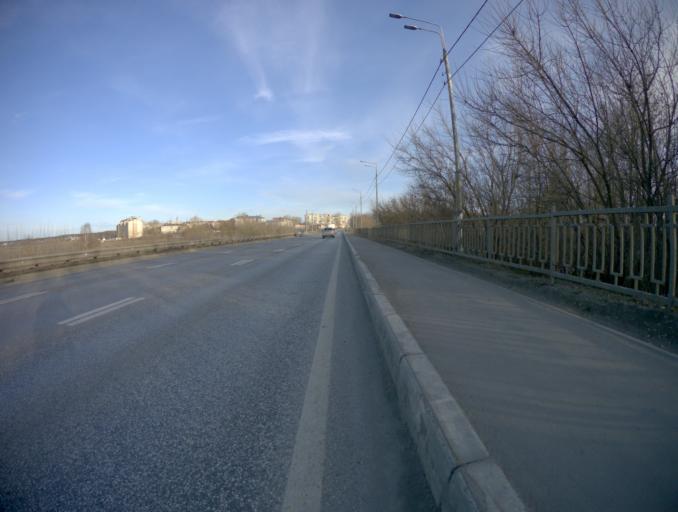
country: RU
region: Vladimir
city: Kommunar
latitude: 56.1131
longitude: 40.4249
